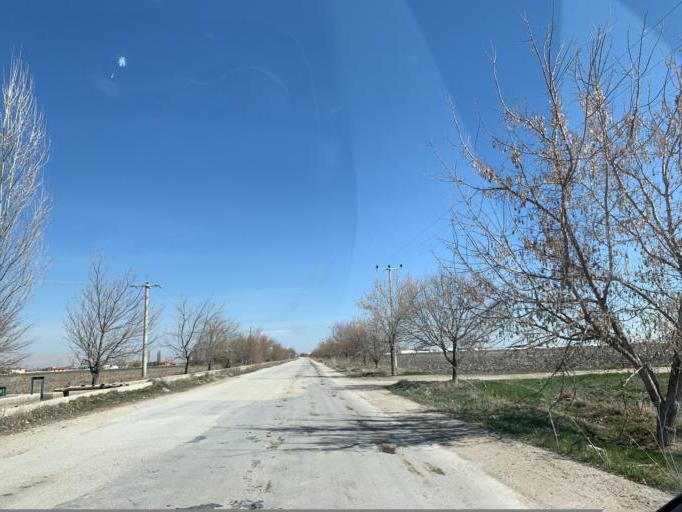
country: TR
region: Konya
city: Catalhoeyuek
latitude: 37.7476
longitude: 32.8330
